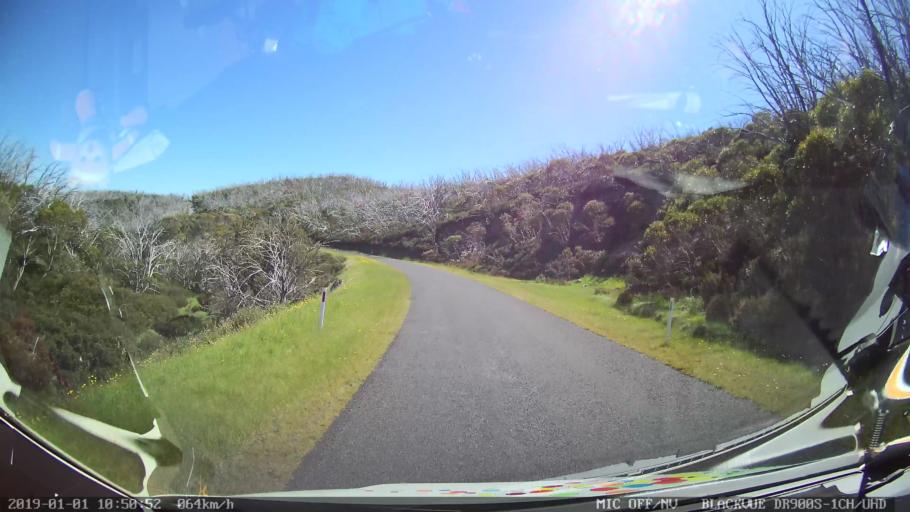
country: AU
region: New South Wales
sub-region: Snowy River
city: Jindabyne
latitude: -36.0243
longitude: 148.3720
